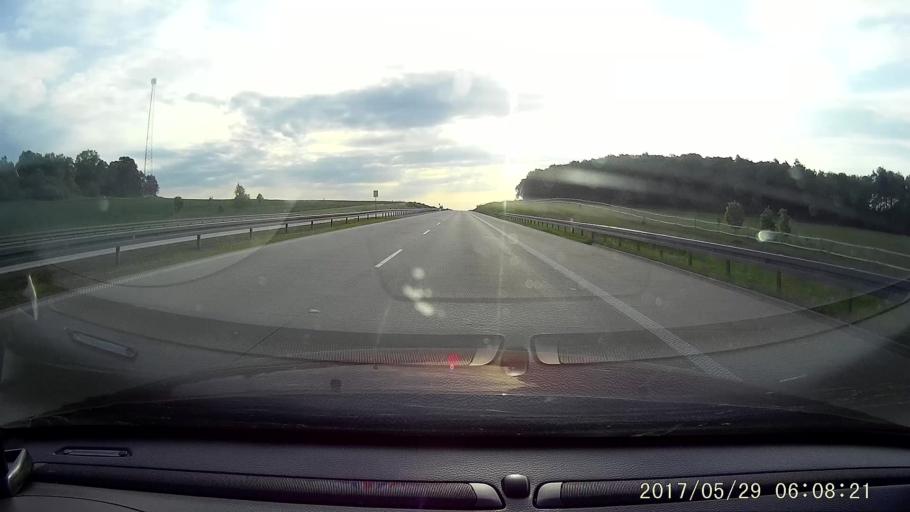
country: PL
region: Lower Silesian Voivodeship
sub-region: Powiat lubanski
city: Siekierczyn
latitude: 51.2024
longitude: 15.1466
